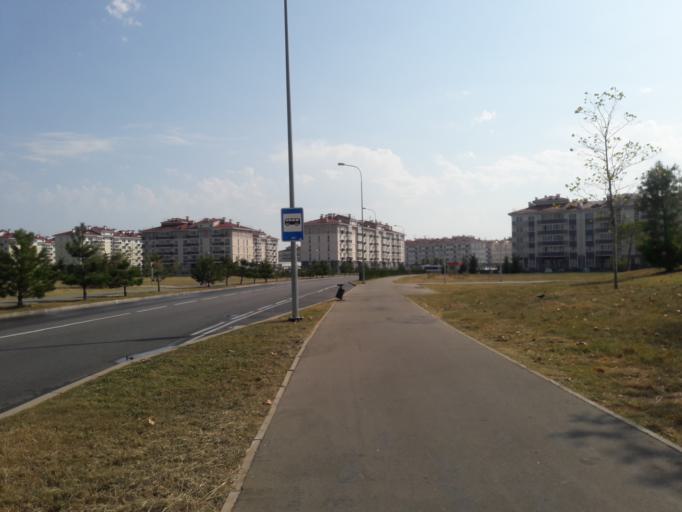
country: RU
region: Krasnodarskiy
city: Vysokoye
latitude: 43.3947
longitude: 39.9960
